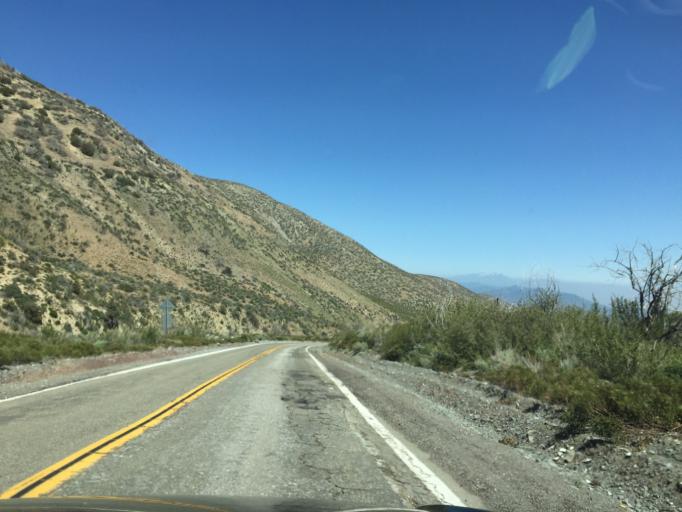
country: US
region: California
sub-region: San Bernardino County
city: Wrightwood
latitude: 34.3382
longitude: -117.5960
